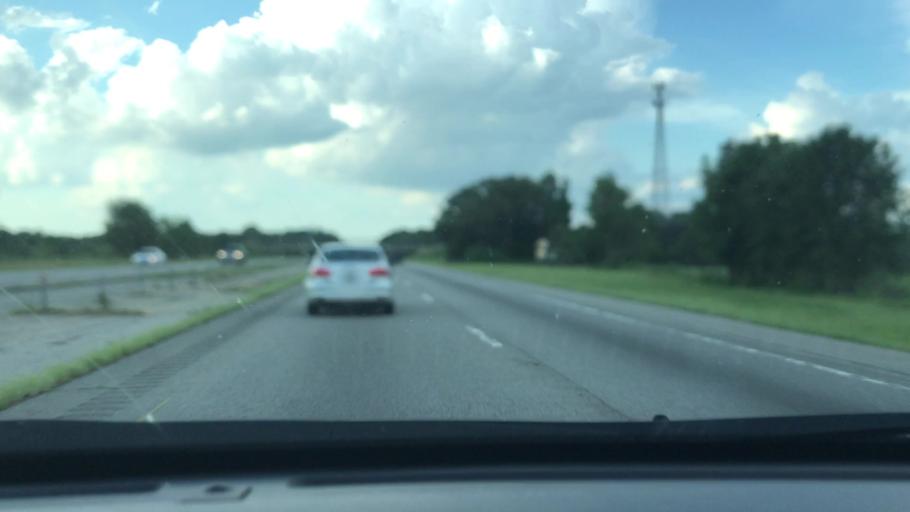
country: US
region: North Carolina
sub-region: Robeson County
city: Saint Pauls
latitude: 34.8774
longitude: -78.9623
